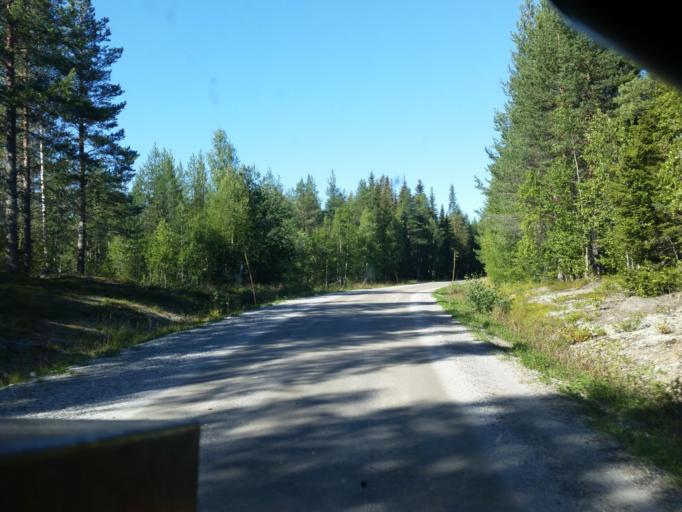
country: SE
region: Vaesterbotten
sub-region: Skelleftea Kommun
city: Storvik
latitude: 65.2176
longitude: 20.9016
